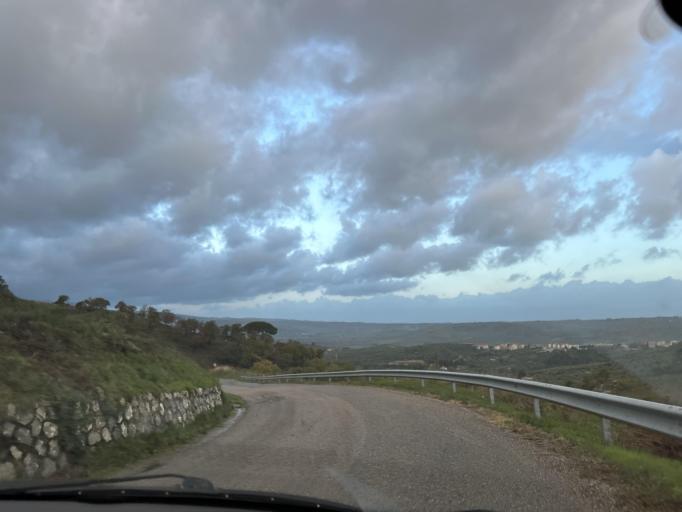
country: IT
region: Calabria
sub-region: Provincia di Catanzaro
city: Squillace
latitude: 38.7659
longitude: 16.5166
